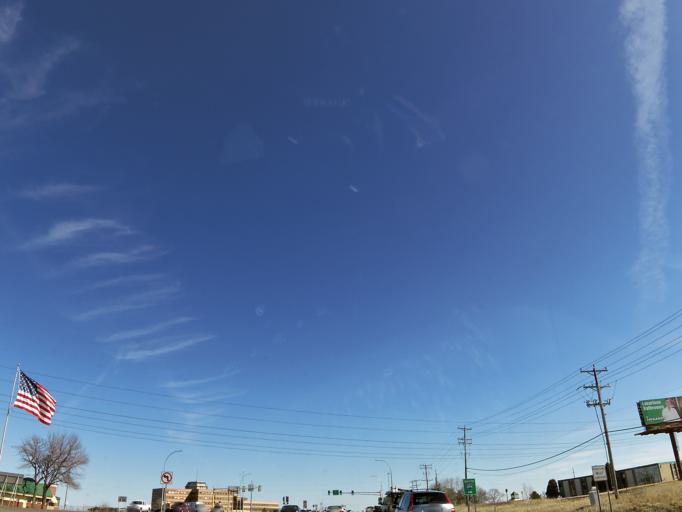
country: US
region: Minnesota
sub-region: Hennepin County
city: Plymouth
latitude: 45.0117
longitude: -93.4602
